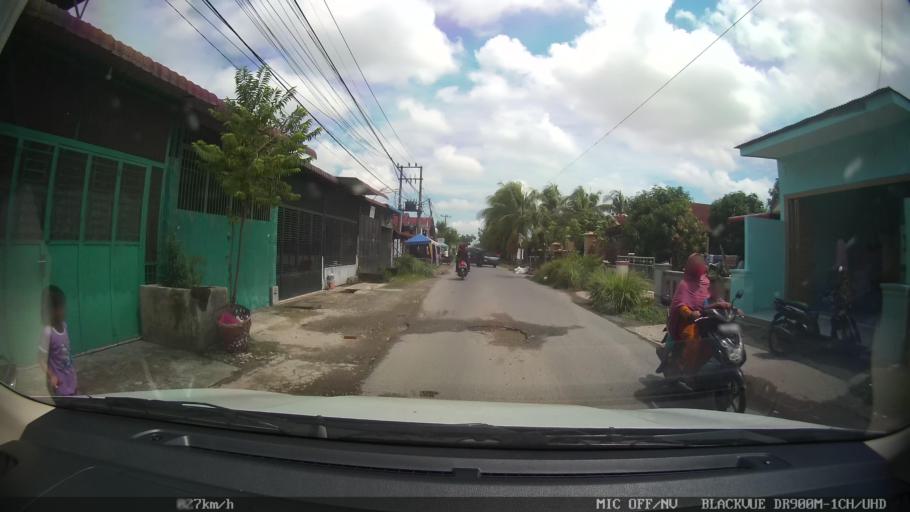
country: ID
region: North Sumatra
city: Percut
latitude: 3.6087
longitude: 98.7815
